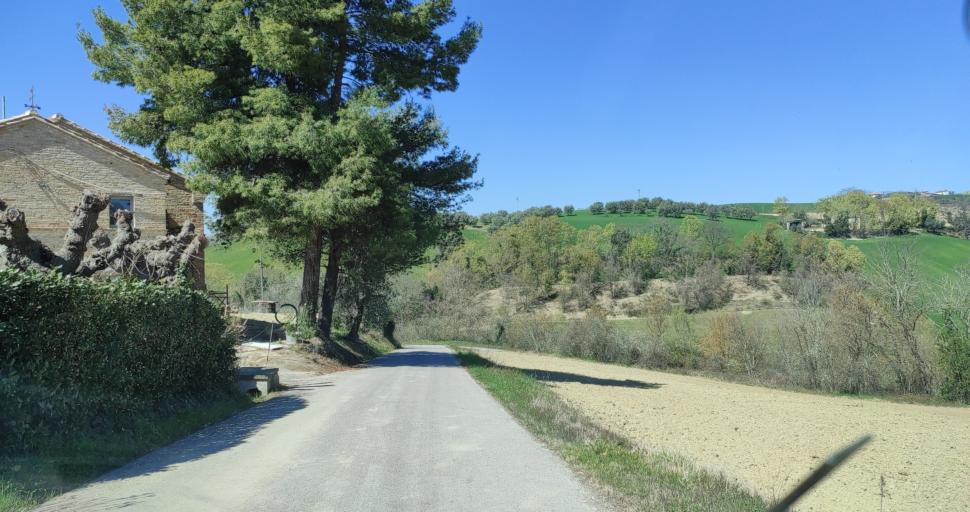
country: IT
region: The Marches
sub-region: Provincia di Macerata
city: Piediripa
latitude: 43.3124
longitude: 13.5025
